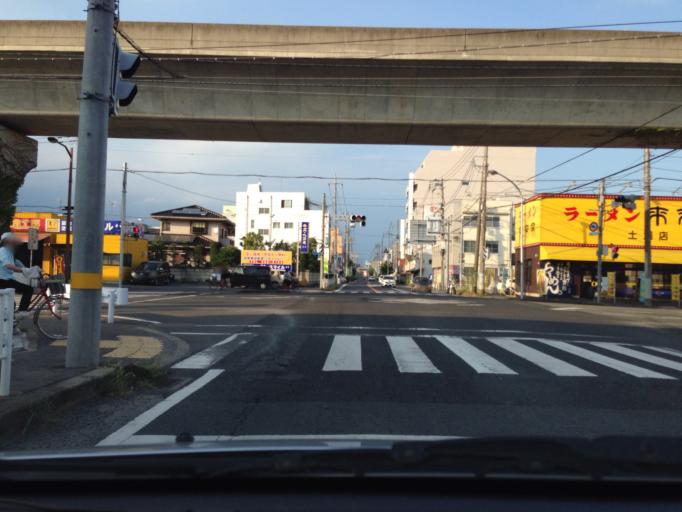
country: JP
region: Ibaraki
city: Naka
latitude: 36.0820
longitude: 140.1932
